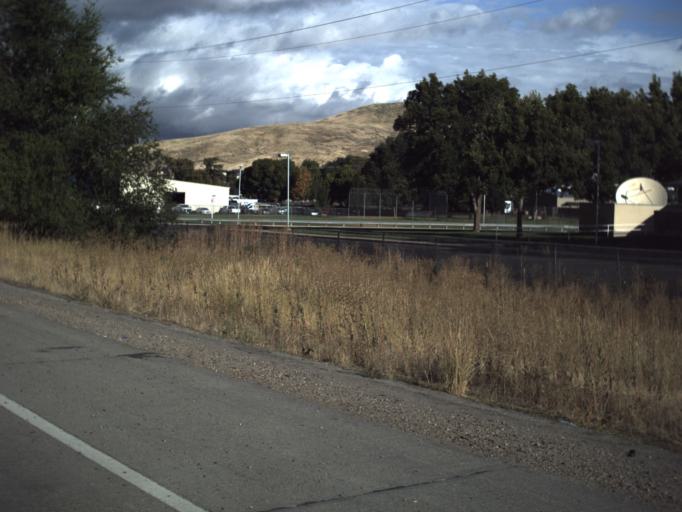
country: US
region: Utah
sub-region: Morgan County
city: Morgan
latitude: 41.0476
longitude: -111.6753
